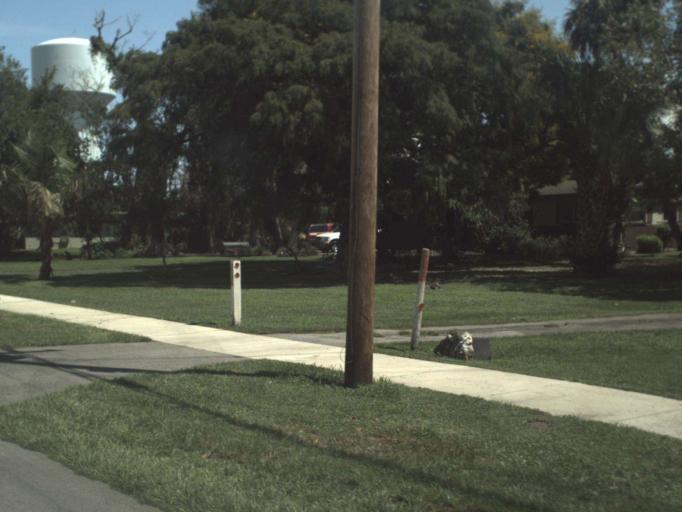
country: US
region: Florida
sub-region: Palm Beach County
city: Pahokee
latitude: 26.8390
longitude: -80.6468
